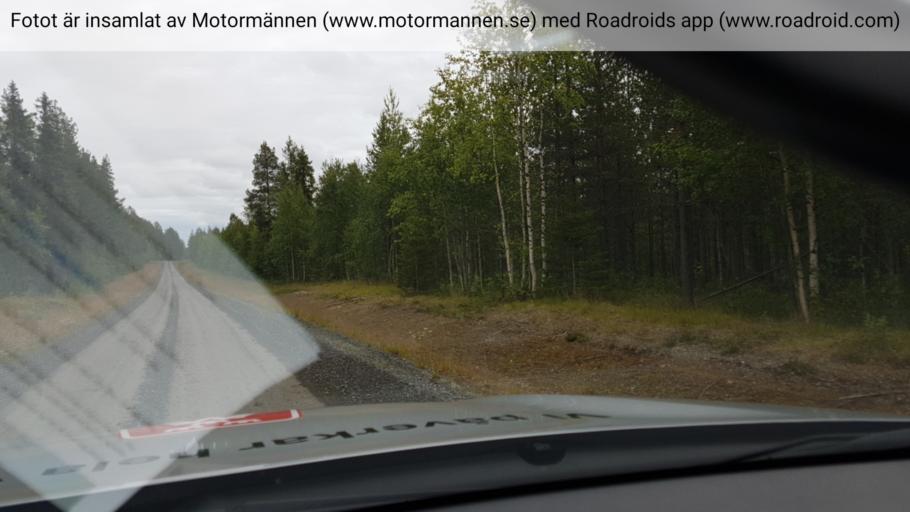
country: SE
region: Norrbotten
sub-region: Pajala Kommun
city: Pajala
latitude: 67.1256
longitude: 22.6733
